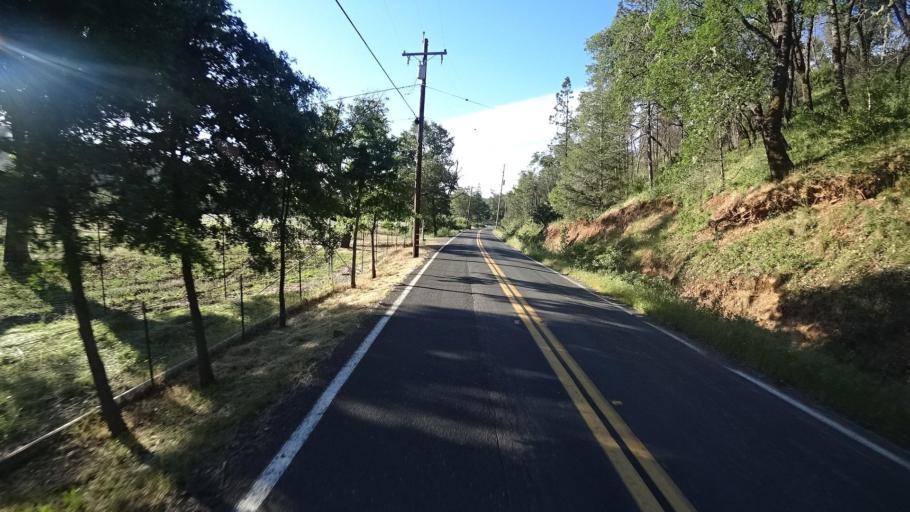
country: US
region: California
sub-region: Lake County
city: Upper Lake
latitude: 39.2112
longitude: -122.9303
